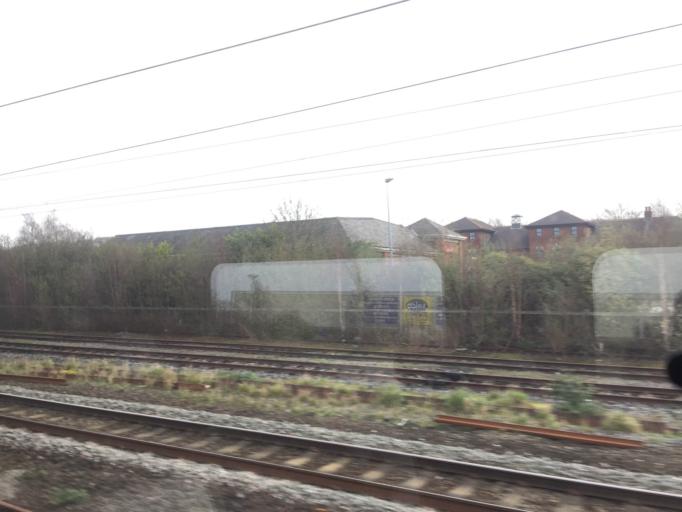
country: GB
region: England
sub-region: Warrington
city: Warrington
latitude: 53.3893
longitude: -2.6039
